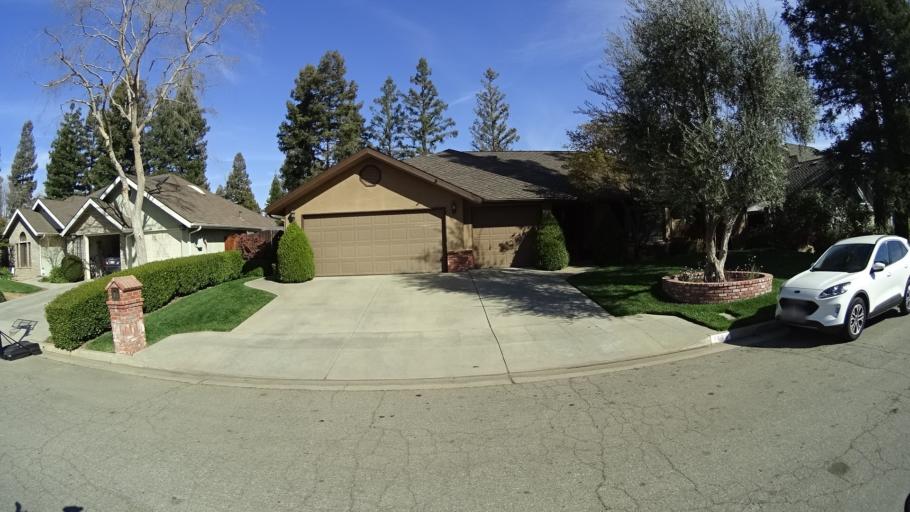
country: US
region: California
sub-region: Fresno County
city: Clovis
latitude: 36.8580
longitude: -119.7534
